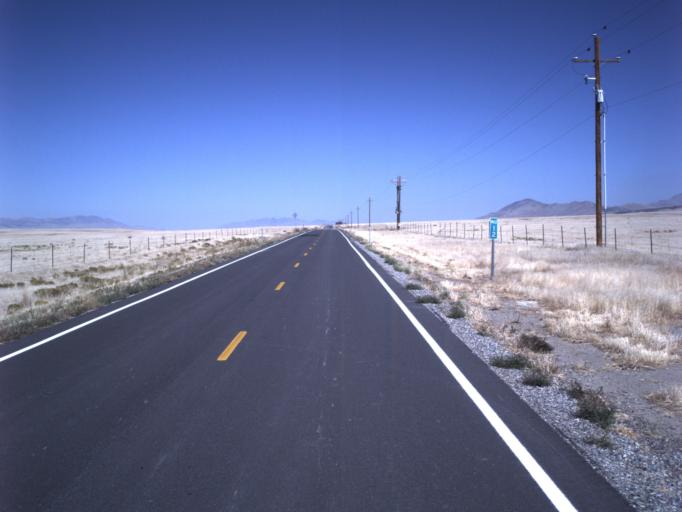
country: US
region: Utah
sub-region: Tooele County
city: Grantsville
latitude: 40.3978
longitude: -112.7478
